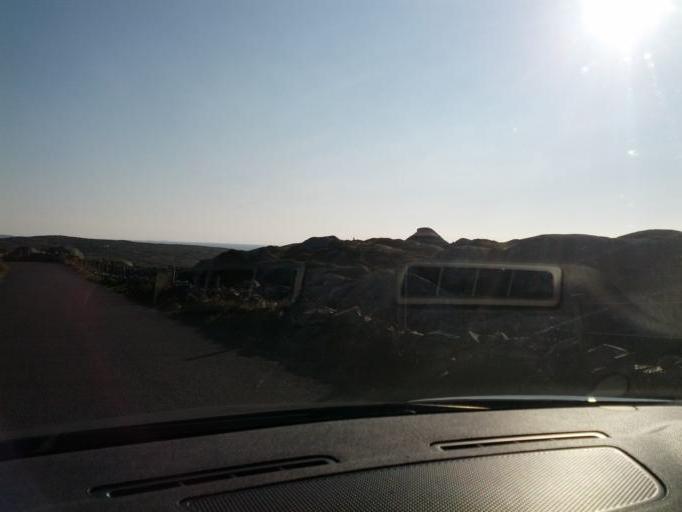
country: IE
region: Connaught
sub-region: County Galway
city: Clifden
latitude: 53.3628
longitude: -9.8798
